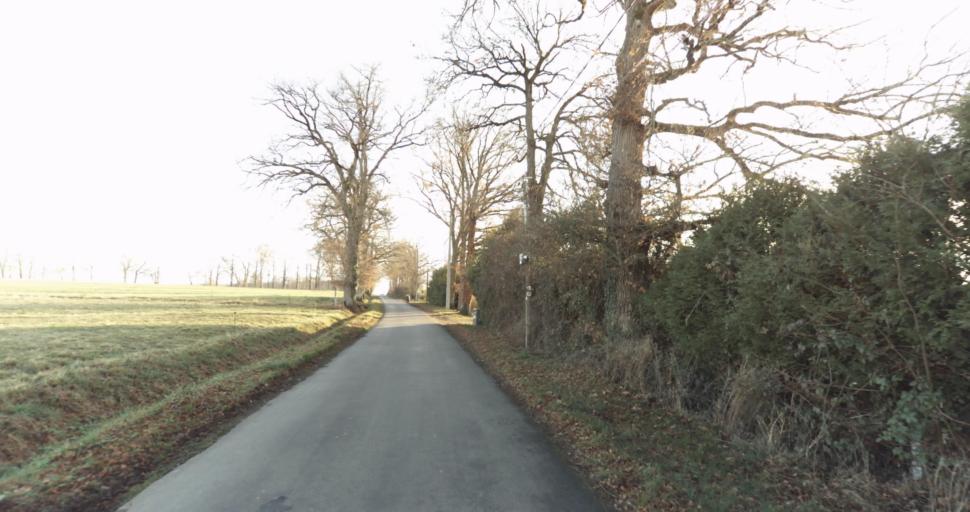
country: FR
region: Limousin
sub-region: Departement de la Haute-Vienne
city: Aixe-sur-Vienne
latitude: 45.7812
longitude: 1.1412
